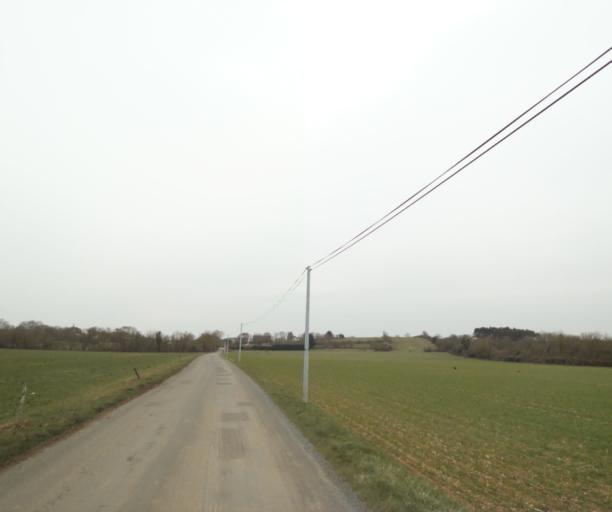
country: FR
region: Poitou-Charentes
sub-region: Departement des Deux-Sevres
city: Magne
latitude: 46.3313
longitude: -0.5274
